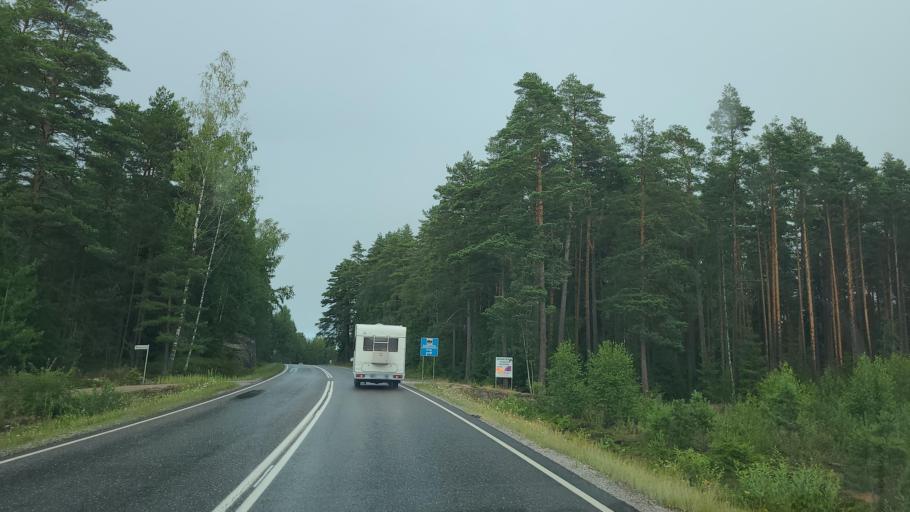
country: FI
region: Varsinais-Suomi
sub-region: Turku
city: Sauvo
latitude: 60.3194
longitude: 22.7066
